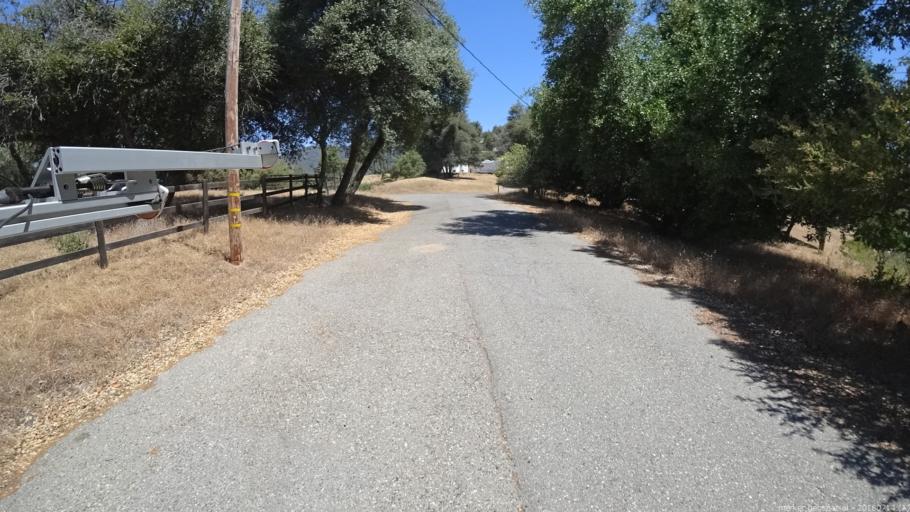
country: US
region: California
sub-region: Madera County
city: Ahwahnee
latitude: 37.4025
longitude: -119.7048
